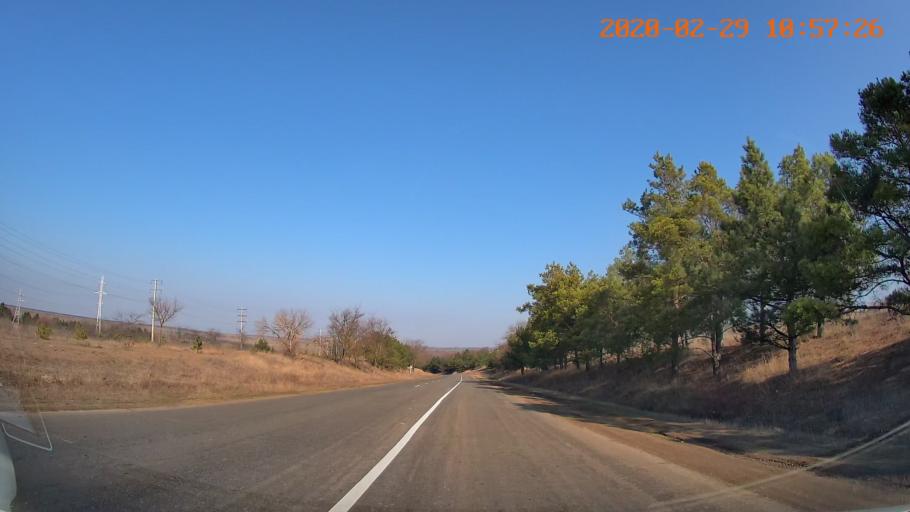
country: MD
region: Telenesti
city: Grigoriopol
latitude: 47.1592
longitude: 29.3218
